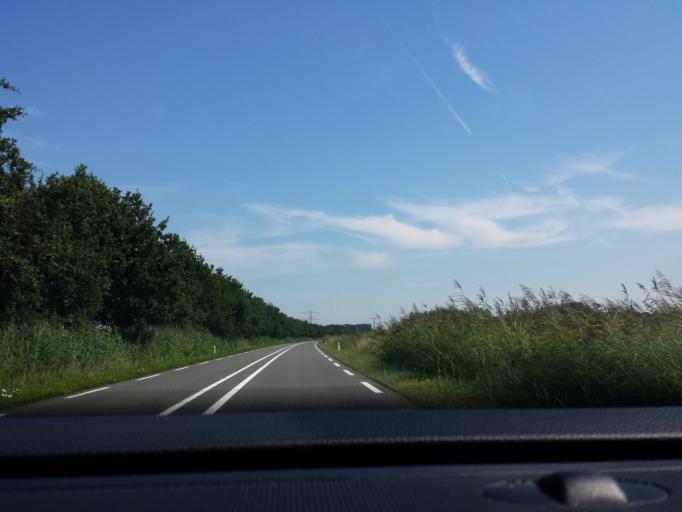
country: NL
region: Overijssel
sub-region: Gemeente Hof van Twente
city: Diepenheim
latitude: 52.2175
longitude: 6.5506
